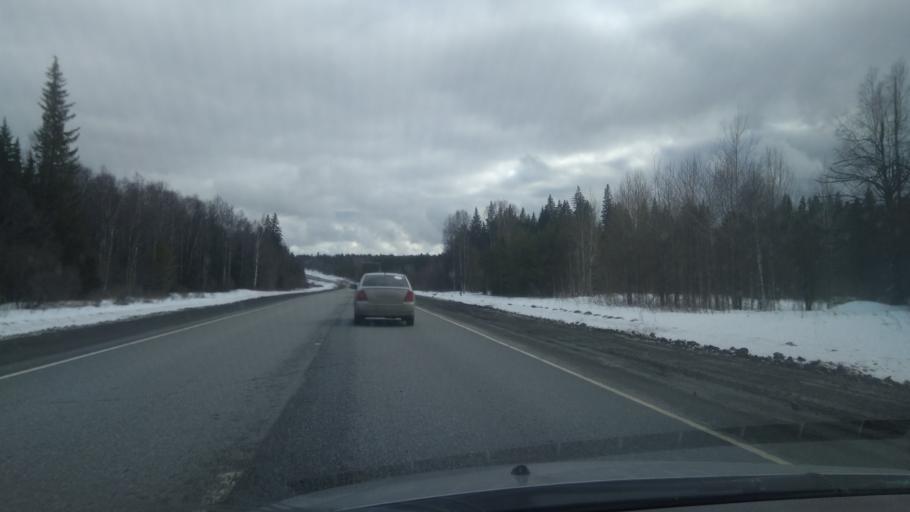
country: RU
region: Sverdlovsk
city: Atig
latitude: 56.8078
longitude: 59.3687
